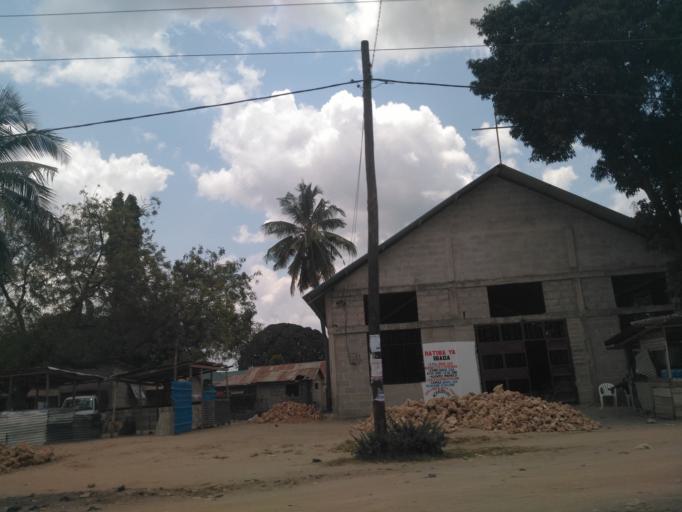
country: TZ
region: Dar es Salaam
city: Dar es Salaam
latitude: -6.8417
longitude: 39.3203
